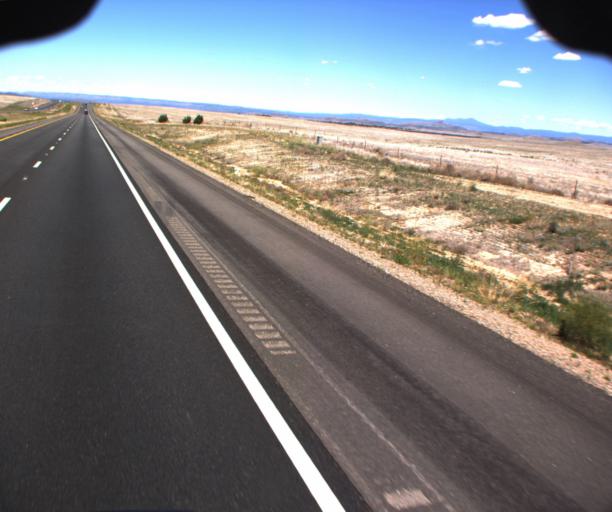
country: US
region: Arizona
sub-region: Yavapai County
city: Chino Valley
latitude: 34.6877
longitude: -112.4452
